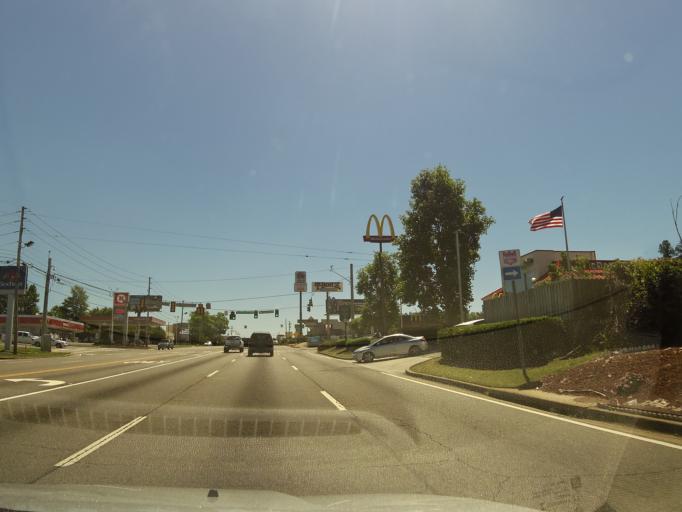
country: US
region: Georgia
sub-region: Columbia County
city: Martinez
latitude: 33.5115
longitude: -82.0390
